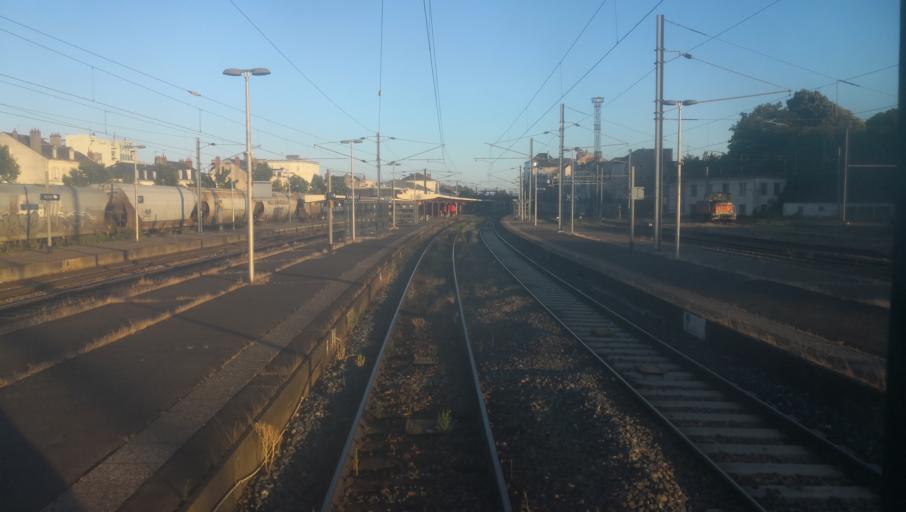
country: FR
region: Bourgogne
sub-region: Departement de la Nievre
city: Nevers
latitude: 46.9888
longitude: 3.1497
